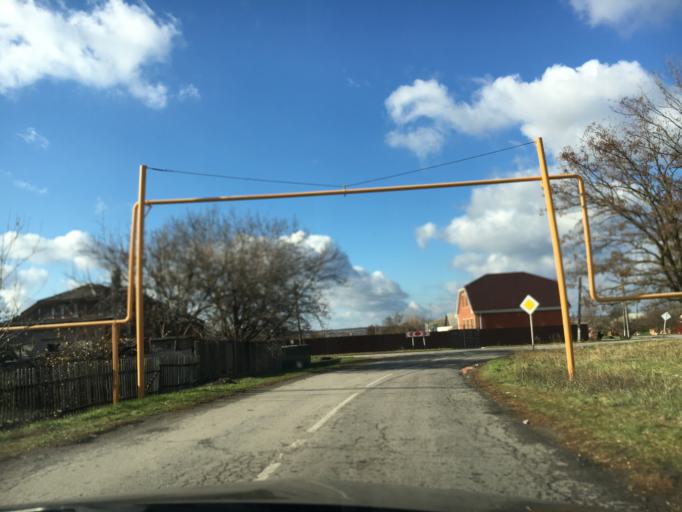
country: RU
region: Rostov
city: Pokrovskoye
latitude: 47.4805
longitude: 38.9190
